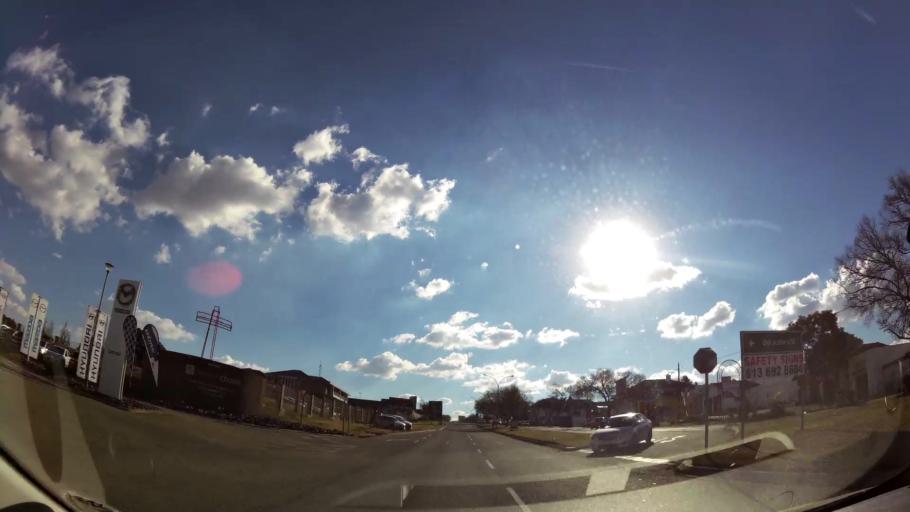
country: ZA
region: Mpumalanga
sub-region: Nkangala District Municipality
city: Witbank
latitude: -25.8760
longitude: 29.2418
